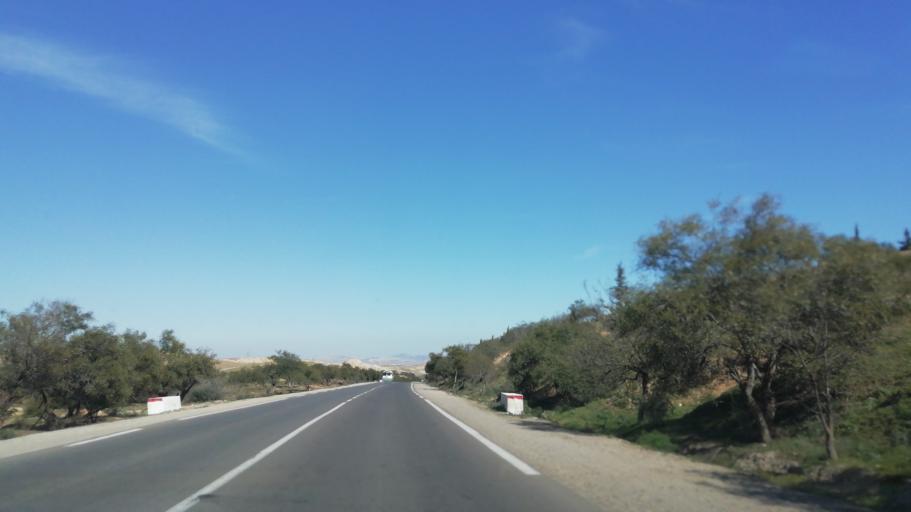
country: DZ
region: Mascara
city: Oued el Abtal
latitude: 35.4363
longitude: 0.4964
